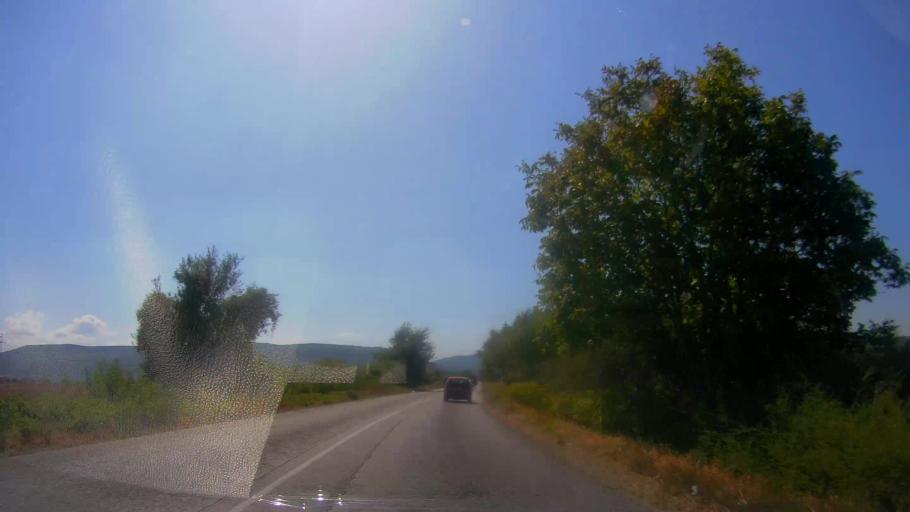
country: BG
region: Veliko Turnovo
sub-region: Obshtina Gorna Oryakhovitsa
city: Purvomaytsi
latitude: 43.1613
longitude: 25.6196
